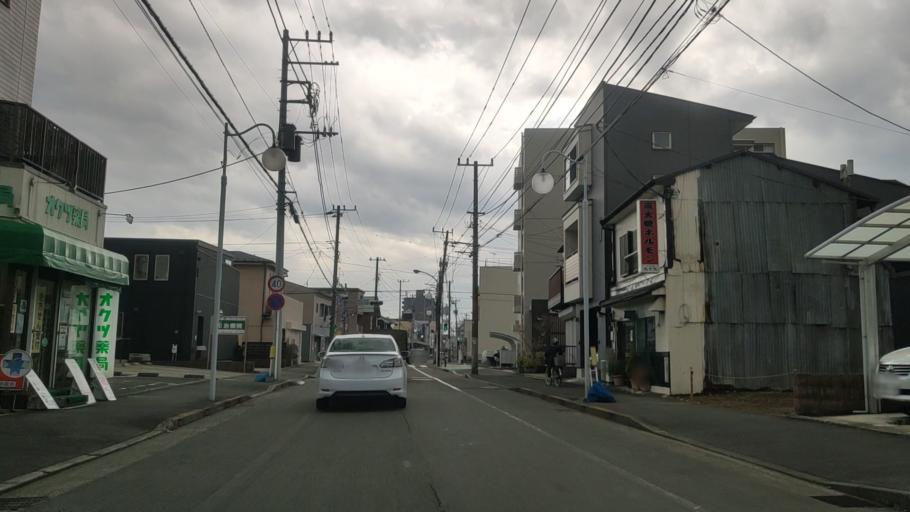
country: JP
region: Kanagawa
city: Odawara
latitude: 35.2569
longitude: 139.1613
